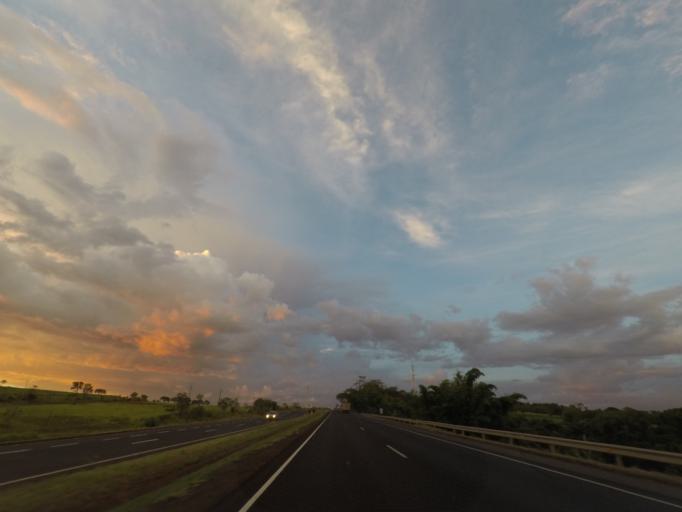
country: BR
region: Minas Gerais
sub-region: Uberaba
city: Uberaba
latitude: -19.5913
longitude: -48.0286
